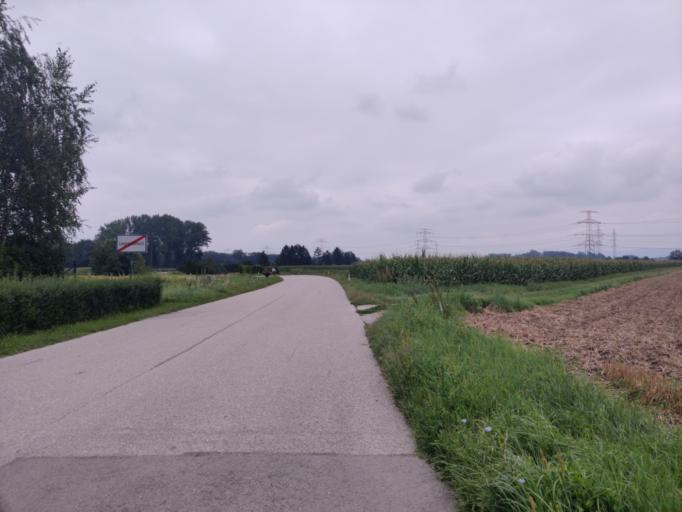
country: AT
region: Lower Austria
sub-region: Politischer Bezirk Tulln
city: Langenrohr
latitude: 48.3281
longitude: 15.9874
